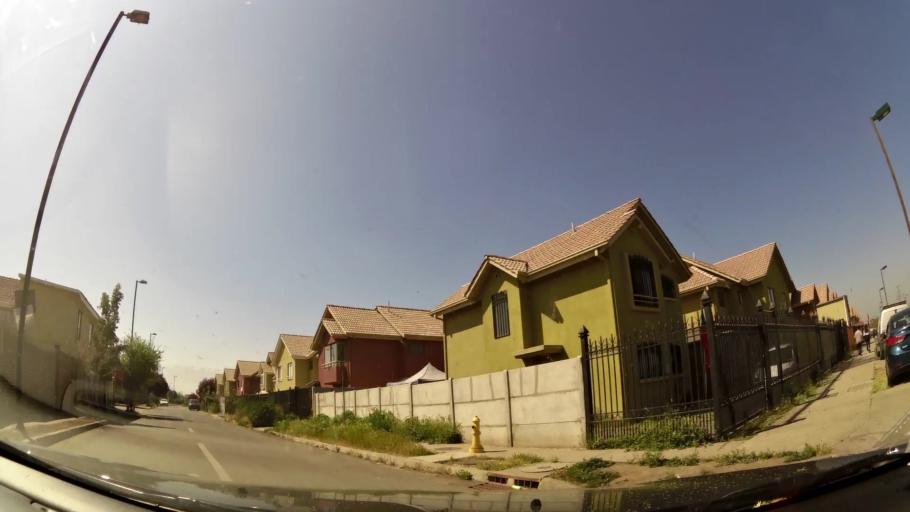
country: CL
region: Santiago Metropolitan
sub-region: Provincia de Chacabuco
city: Chicureo Abajo
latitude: -33.3254
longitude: -70.7546
